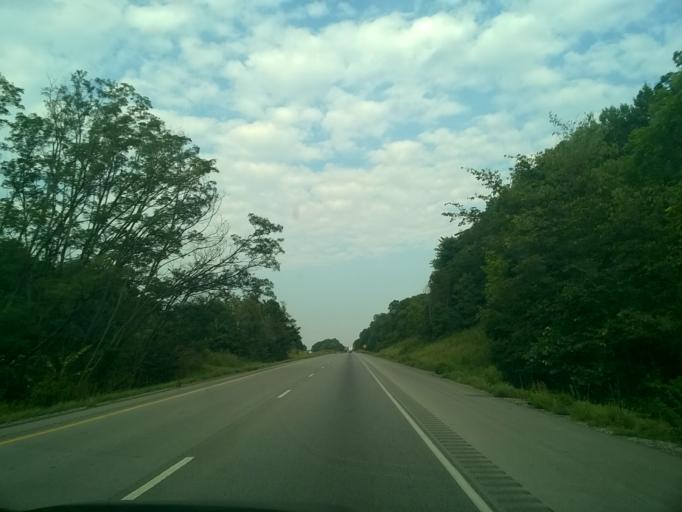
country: US
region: Indiana
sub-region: Putnam County
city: Cloverdale
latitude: 39.5146
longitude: -86.9183
